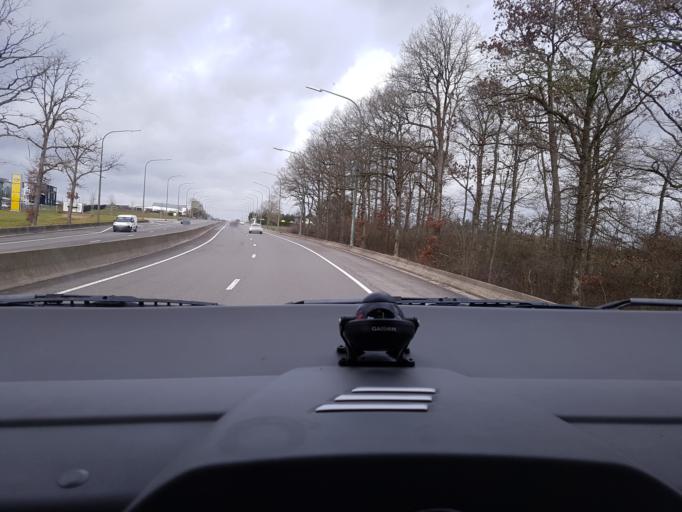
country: BE
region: Wallonia
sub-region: Province du Luxembourg
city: Marche-en-Famenne
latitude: 50.2410
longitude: 5.2918
